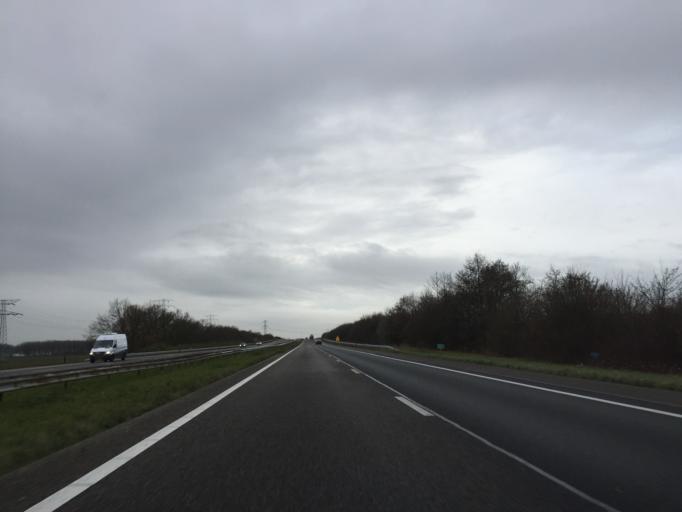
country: NL
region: North Brabant
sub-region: Gemeente Woensdrecht
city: Woensdrecht
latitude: 51.4289
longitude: 4.2476
